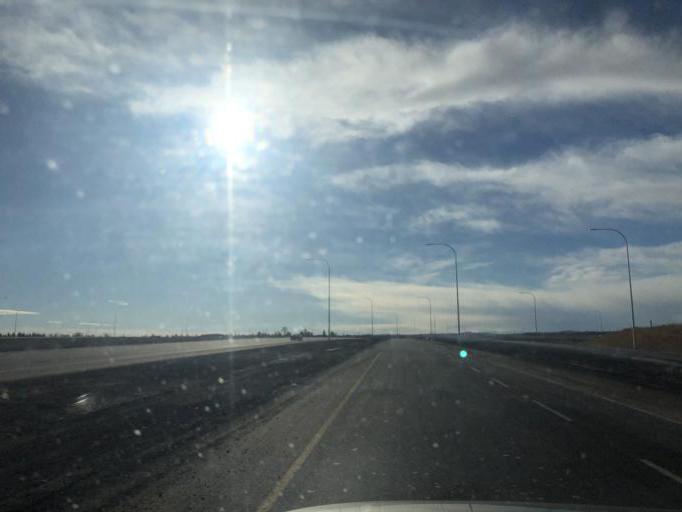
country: CA
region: Alberta
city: Calgary
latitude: 50.9551
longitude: -114.1427
